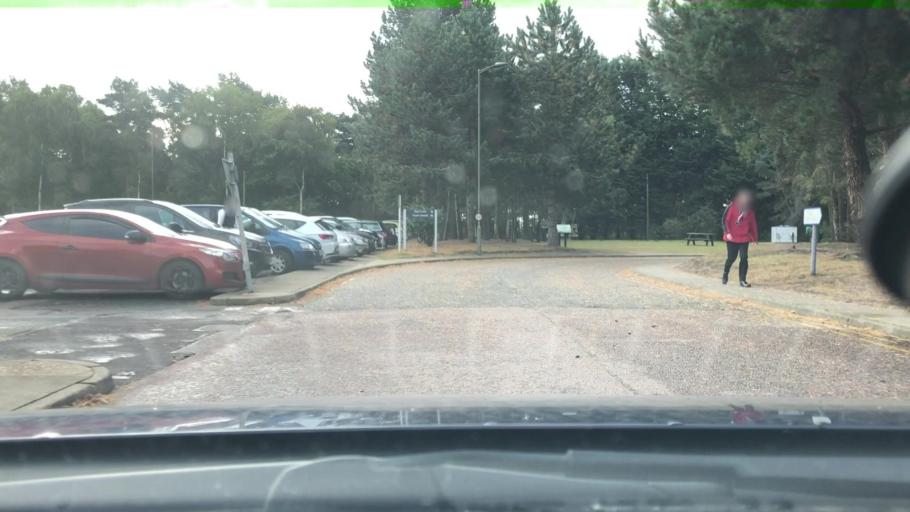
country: GB
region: England
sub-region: Suffolk
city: Kesgrave
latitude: 52.0562
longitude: 1.2837
